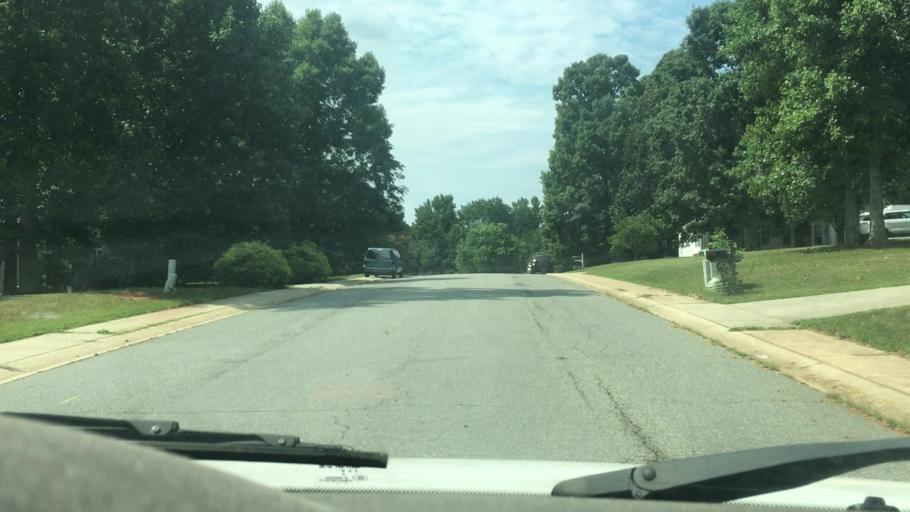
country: US
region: North Carolina
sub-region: Gaston County
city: Davidson
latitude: 35.5380
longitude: -80.8298
